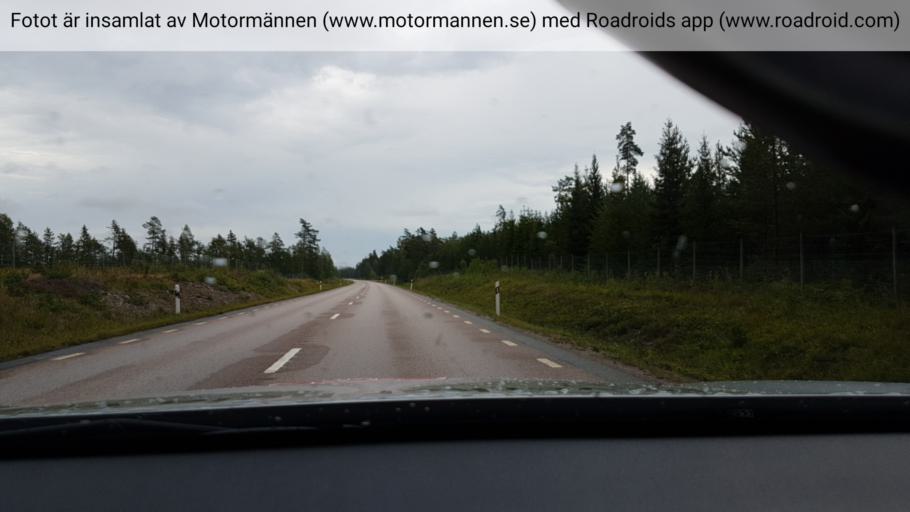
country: SE
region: Uppsala
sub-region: Tierps Kommun
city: Karlholmsbruk
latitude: 60.4291
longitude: 17.8207
